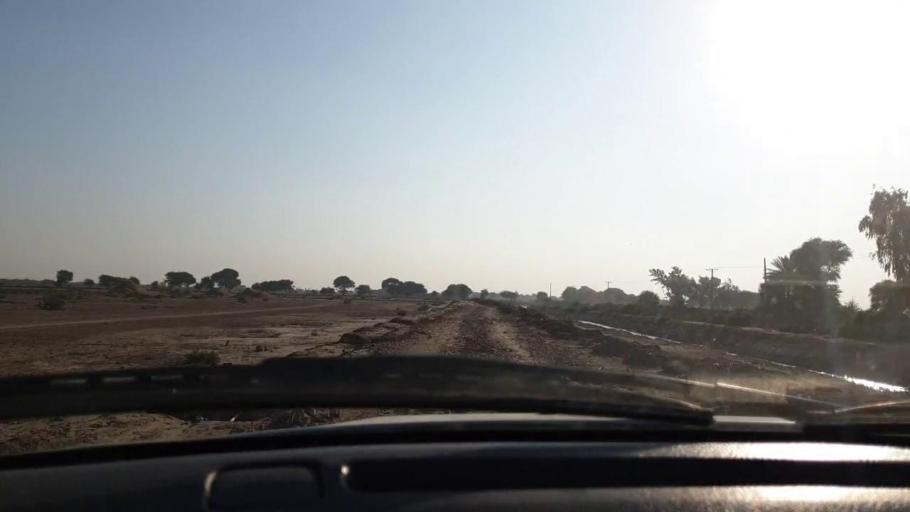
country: PK
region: Sindh
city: Bulri
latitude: 24.8111
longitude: 68.3984
